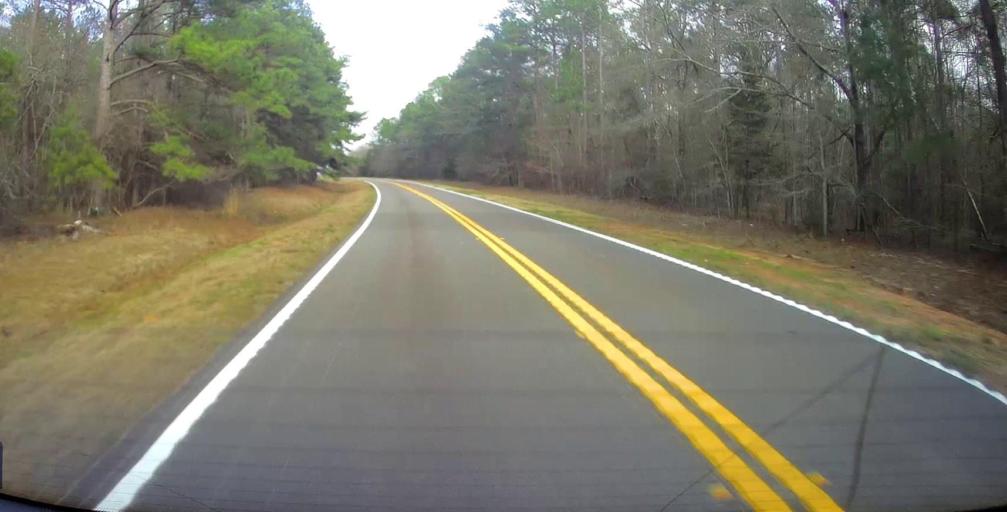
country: US
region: Georgia
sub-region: Marion County
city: Buena Vista
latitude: 32.4419
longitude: -84.4788
